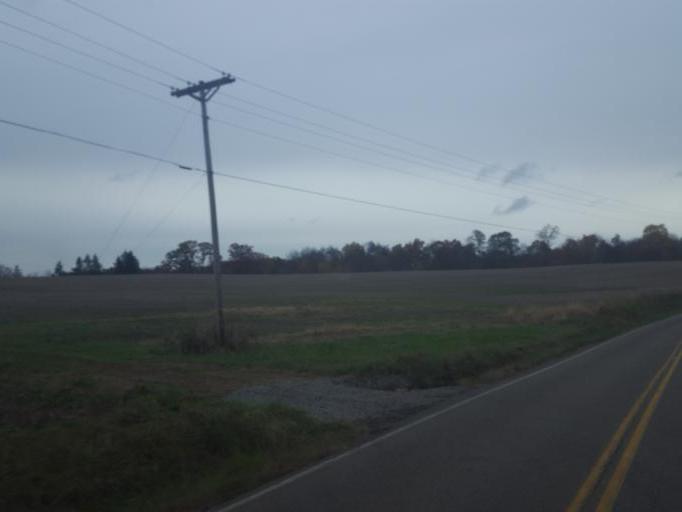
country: US
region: Ohio
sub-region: Knox County
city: Oak Hill
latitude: 40.4515
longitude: -82.1291
